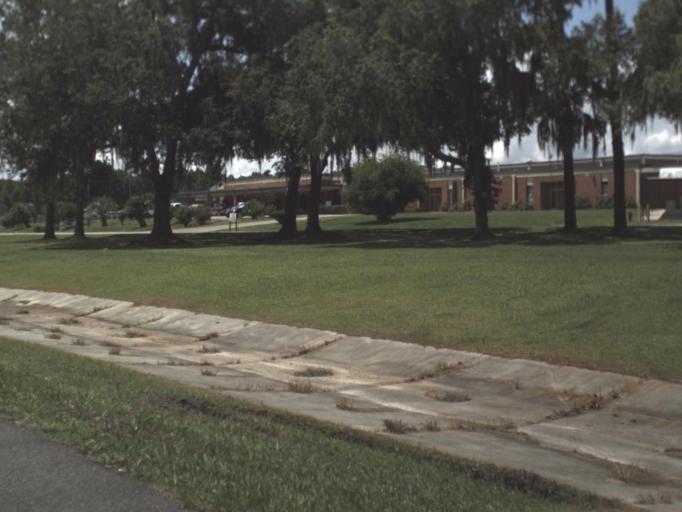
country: US
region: Florida
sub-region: Putnam County
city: Crescent City
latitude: 29.4740
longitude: -81.5353
